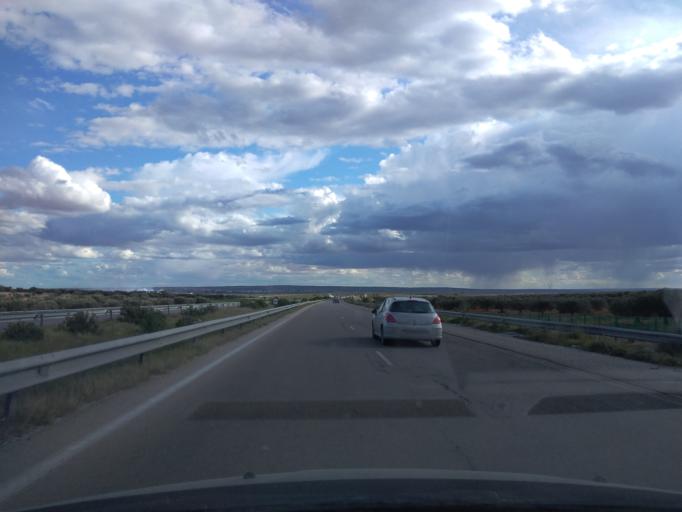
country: TN
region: Al Munastir
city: Manzil Kamil
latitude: 35.5284
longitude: 10.6257
